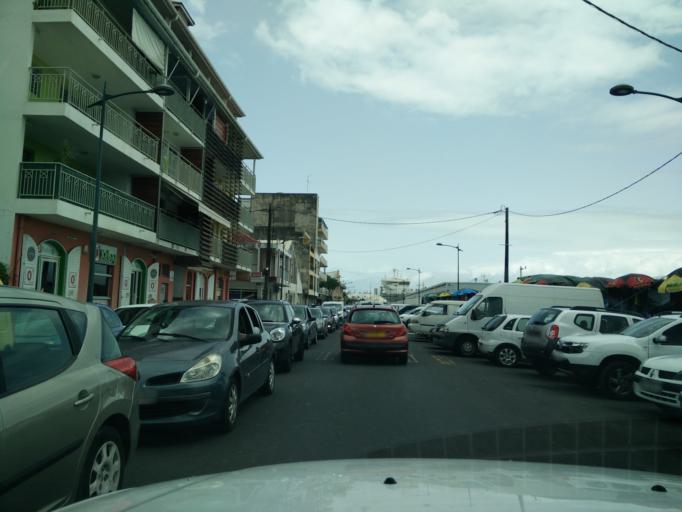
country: GP
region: Guadeloupe
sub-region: Guadeloupe
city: Pointe-a-Pitre
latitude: 16.2404
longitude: -61.5383
